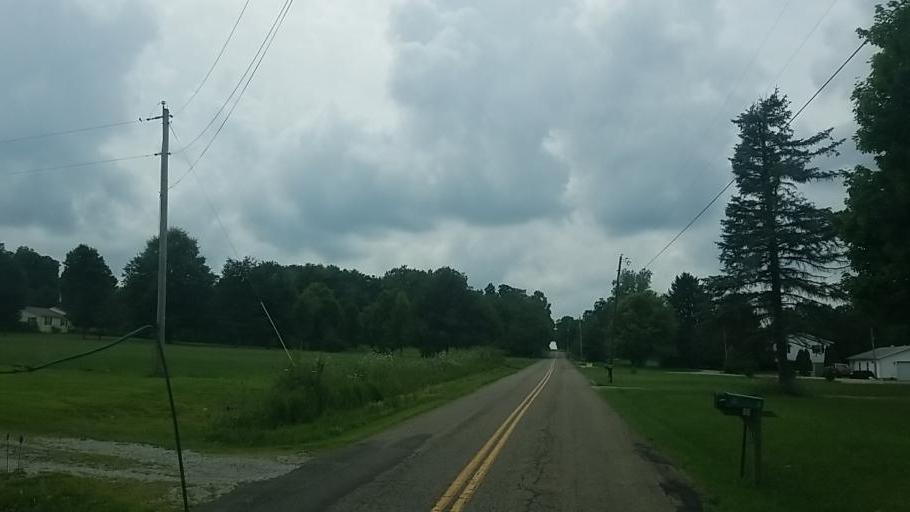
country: US
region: Ohio
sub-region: Knox County
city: Gambier
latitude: 40.3407
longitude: -82.4481
